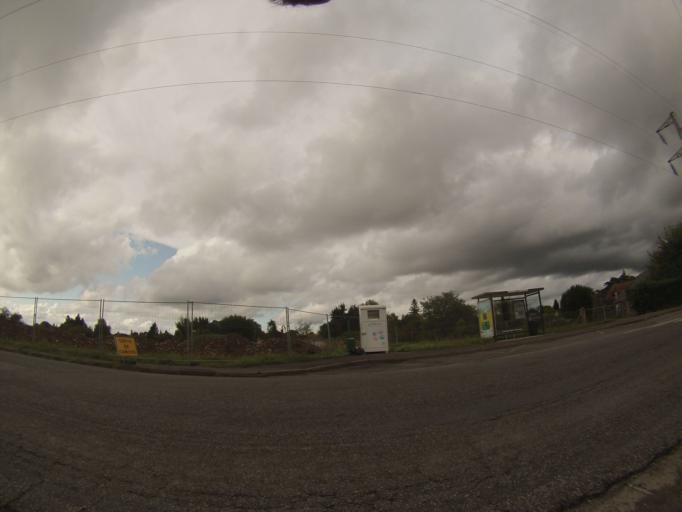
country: FR
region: Aquitaine
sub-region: Departement des Pyrenees-Atlantiques
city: Gelos
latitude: 43.2792
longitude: -0.3657
